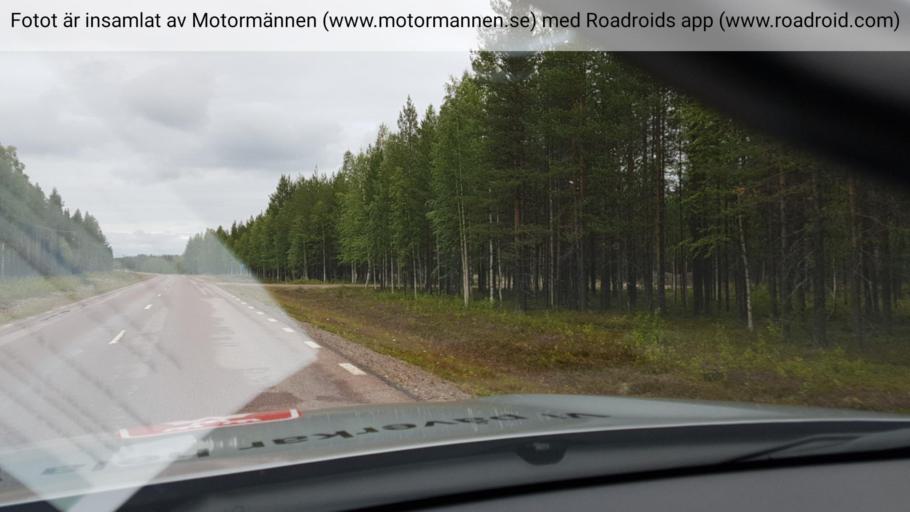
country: SE
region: Norrbotten
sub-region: Pajala Kommun
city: Pajala
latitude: 67.1120
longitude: 22.6019
